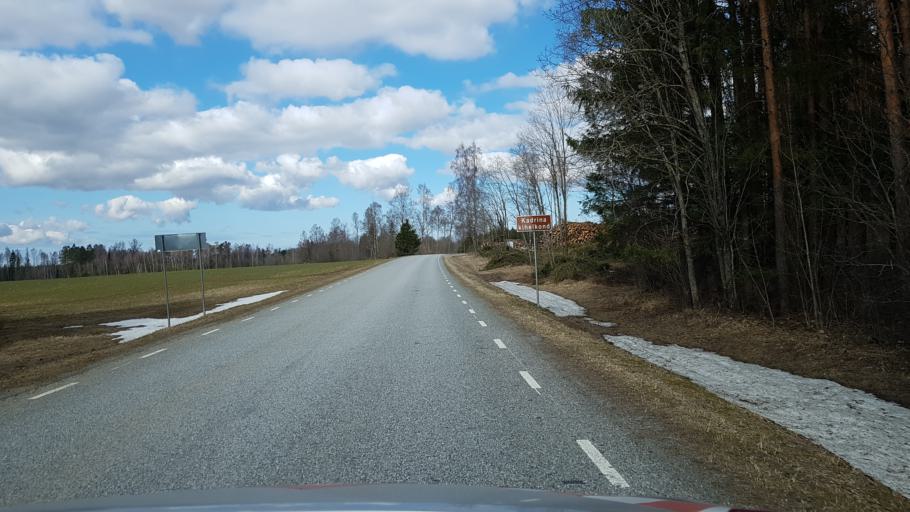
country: EE
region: Laeaene-Virumaa
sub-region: Tamsalu vald
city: Tamsalu
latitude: 59.2188
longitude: 26.1598
